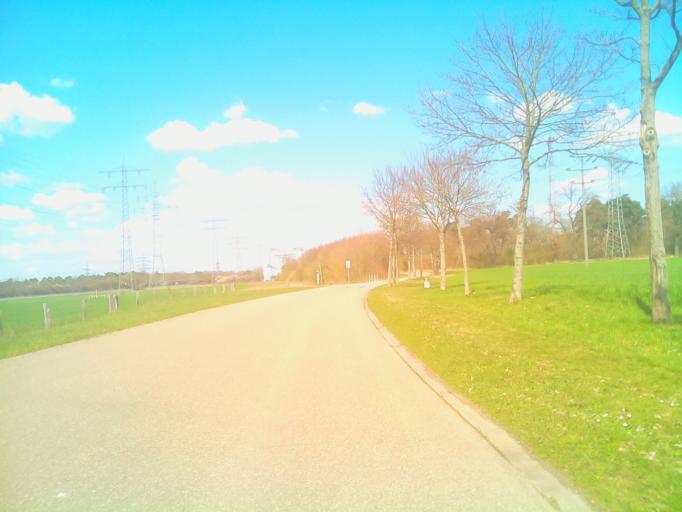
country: DE
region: Baden-Wuerttemberg
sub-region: Karlsruhe Region
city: Bruhl
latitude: 49.4367
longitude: 8.5433
